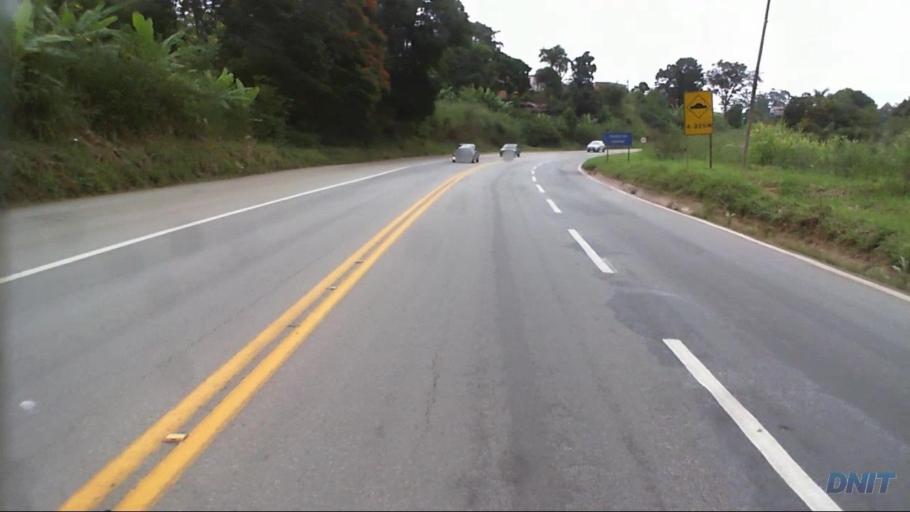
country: BR
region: Minas Gerais
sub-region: Joao Monlevade
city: Joao Monlevade
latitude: -19.8477
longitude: -43.1640
